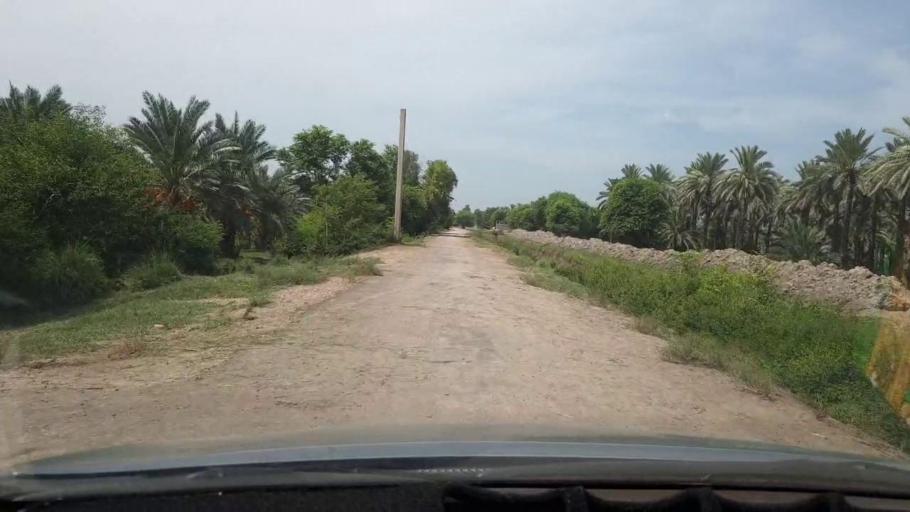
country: PK
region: Sindh
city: Khairpur
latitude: 27.4966
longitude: 68.7469
